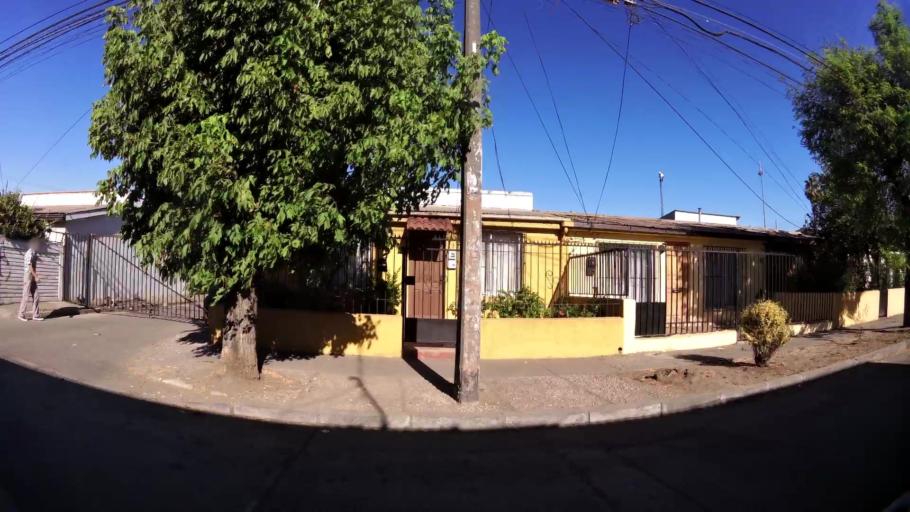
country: CL
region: O'Higgins
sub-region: Provincia de Colchagua
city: Chimbarongo
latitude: -34.5861
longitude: -70.9954
